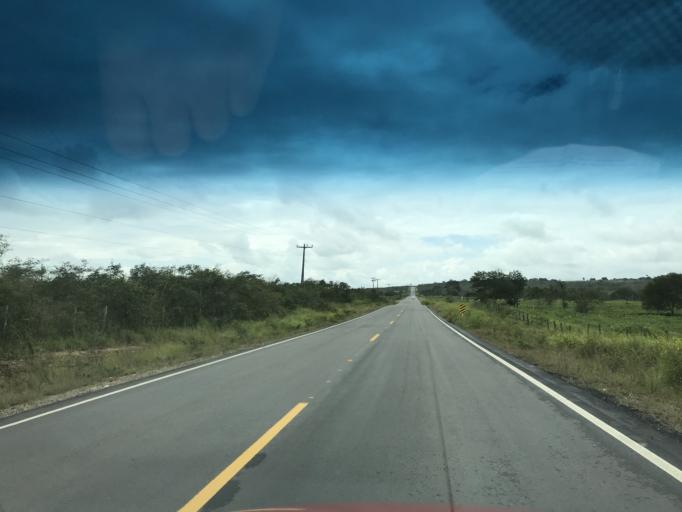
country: BR
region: Bahia
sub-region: Castro Alves
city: Castro Alves
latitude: -12.6745
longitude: -39.2948
